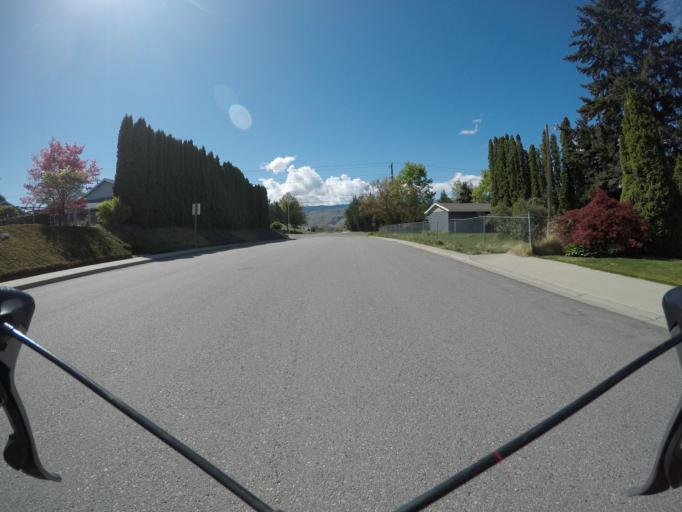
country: US
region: Washington
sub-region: Douglas County
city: East Wenatchee Bench
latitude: 47.4211
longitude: -120.2759
